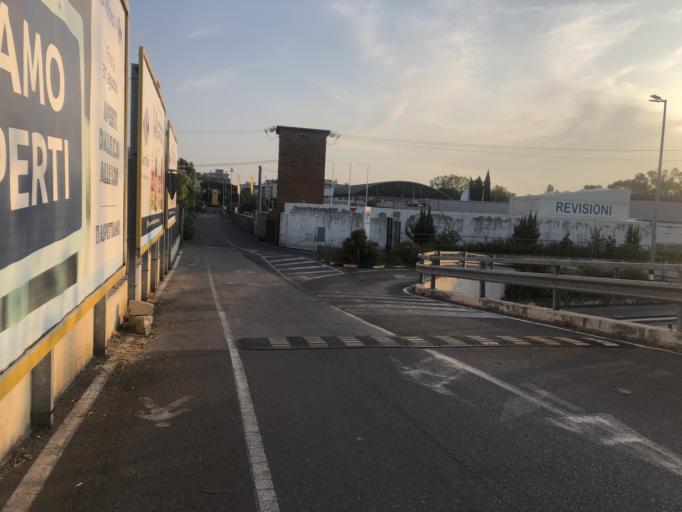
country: IT
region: Tuscany
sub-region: Province of Pisa
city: Pisa
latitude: 43.7249
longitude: 10.4179
